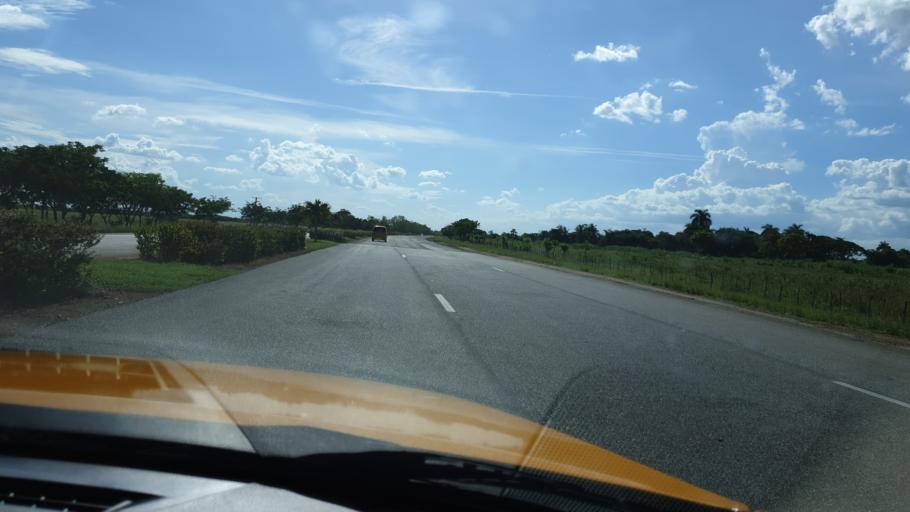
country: CU
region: Cienfuegos
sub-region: Municipio de Aguada de Pasajeros
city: Aguada de Pasajeros
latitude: 22.4095
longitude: -80.8889
